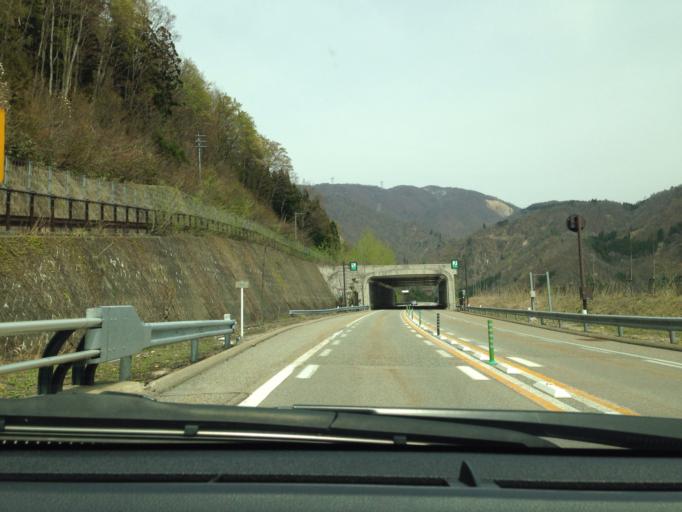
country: JP
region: Toyama
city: Fukumitsu
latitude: 36.2790
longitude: 136.8969
